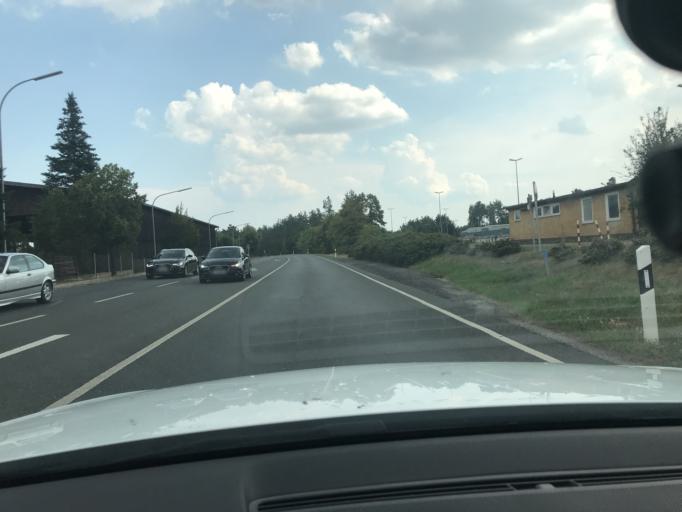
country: DE
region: Bavaria
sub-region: Upper Palatinate
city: Grafenwohr
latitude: 49.7157
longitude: 11.9164
